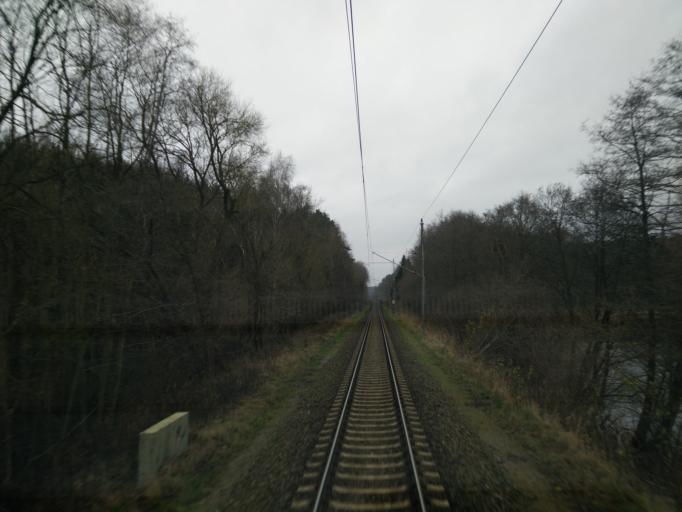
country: DE
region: Mecklenburg-Vorpommern
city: Bad Kleinen
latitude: 53.7970
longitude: 11.4850
